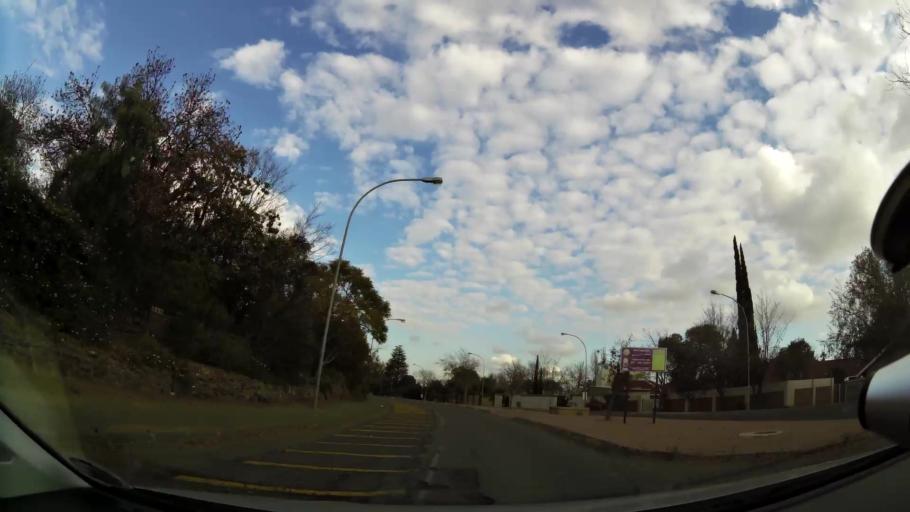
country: ZA
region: Orange Free State
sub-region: Mangaung Metropolitan Municipality
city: Bloemfontein
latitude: -29.0781
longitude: 26.2059
